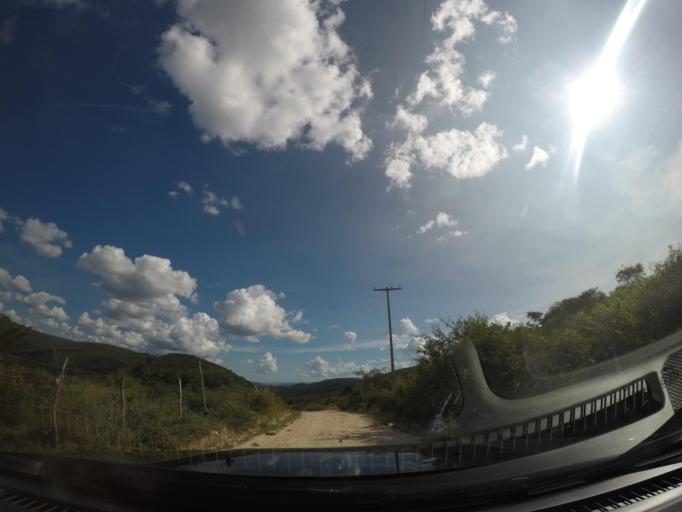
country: BR
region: Bahia
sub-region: Barra Da Estiva
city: Barra da Estiva
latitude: -13.2163
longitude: -41.5946
